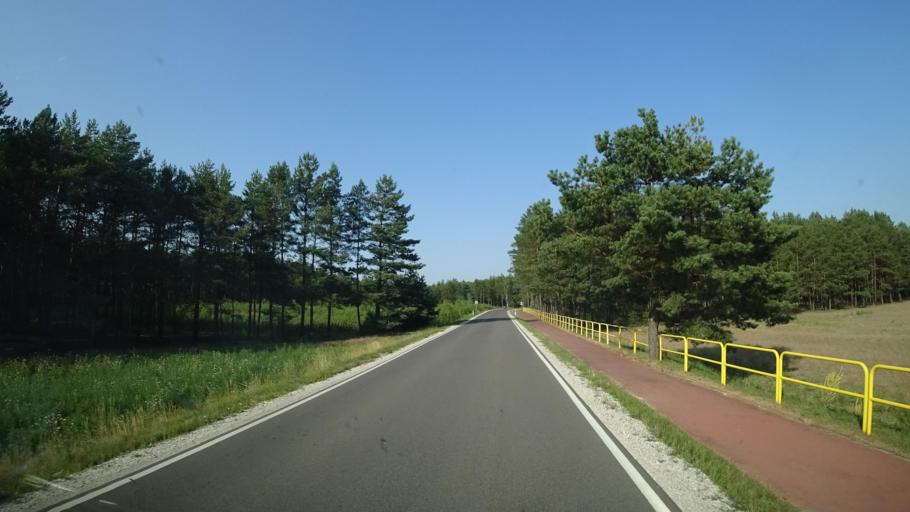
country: PL
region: Pomeranian Voivodeship
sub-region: Powiat bytowski
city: Lipnica
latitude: 53.8468
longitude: 17.4706
